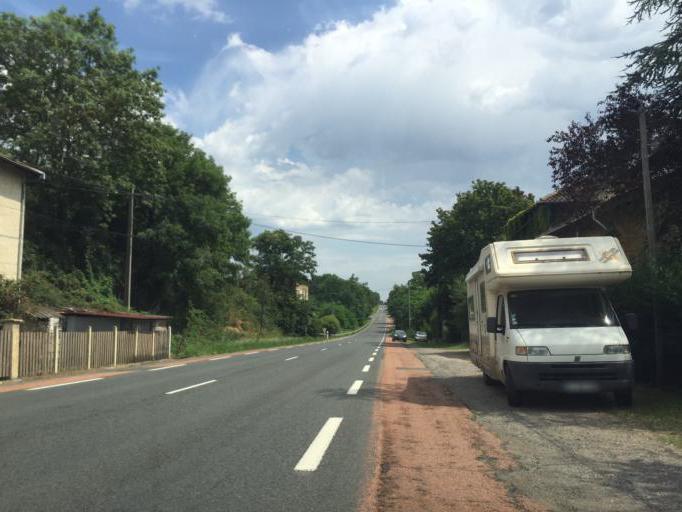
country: FR
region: Rhone-Alpes
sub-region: Departement du Rhone
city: Saint-Romain-de-Popey
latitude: 45.8639
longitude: 4.5528
